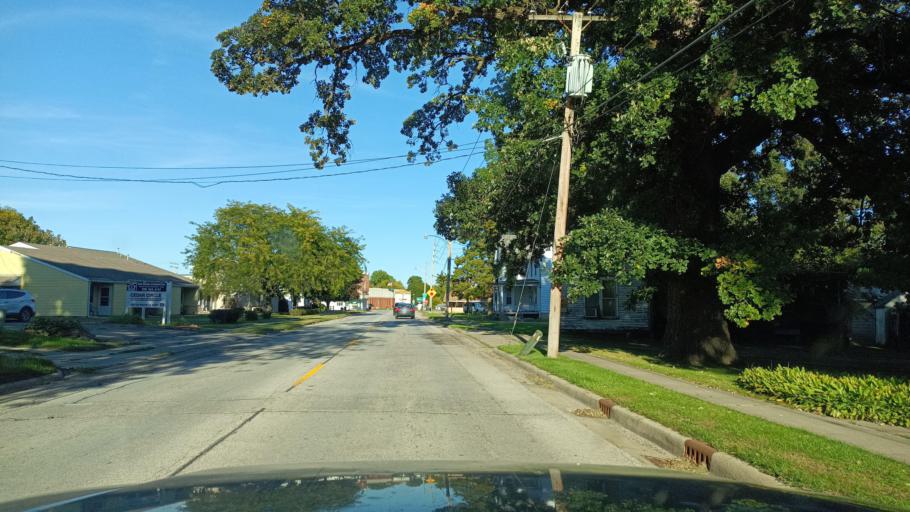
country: US
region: Illinois
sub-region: De Witt County
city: Farmer City
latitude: 40.2410
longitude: -88.6446
